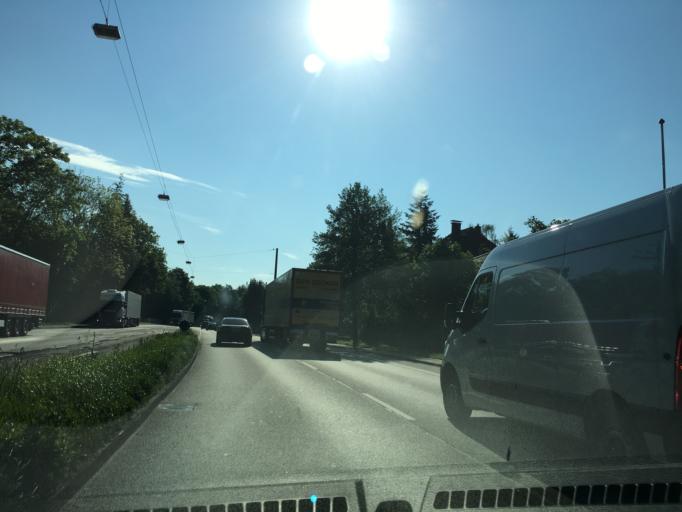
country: DE
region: North Rhine-Westphalia
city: Bad Oeynhausen
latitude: 52.2062
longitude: 8.7917
